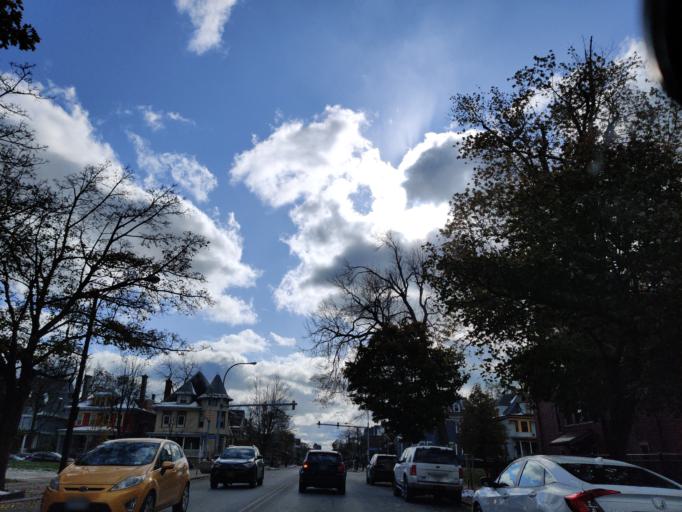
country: US
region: New York
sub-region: Erie County
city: Buffalo
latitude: 42.9209
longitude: -78.8770
